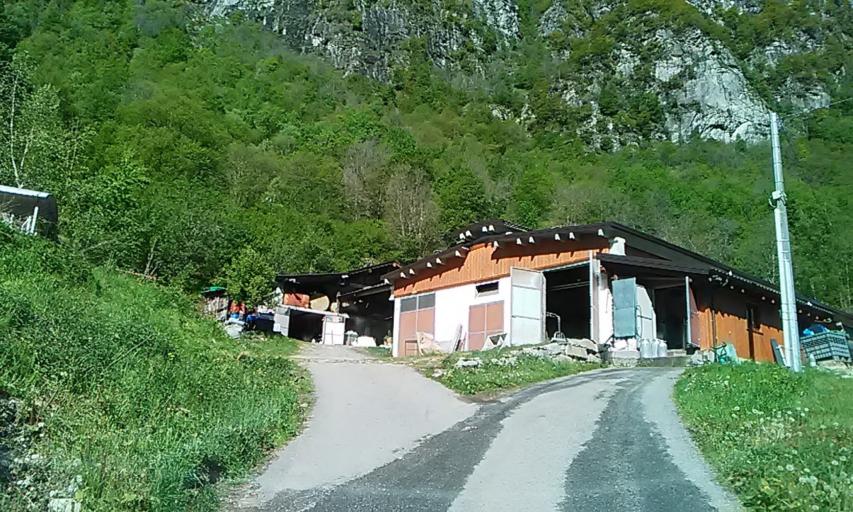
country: IT
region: Piedmont
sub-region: Provincia di Vercelli
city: Campertogno
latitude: 45.7874
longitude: 8.0362
